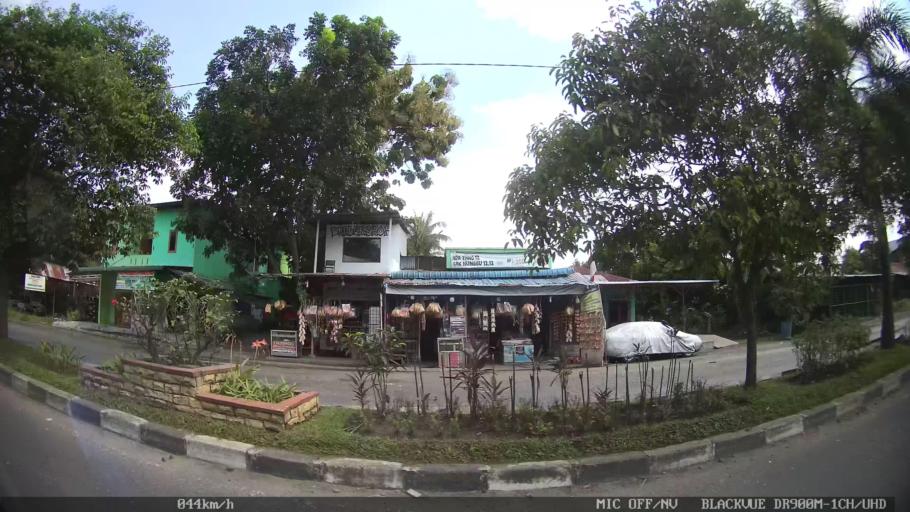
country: ID
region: North Sumatra
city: Binjai
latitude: 3.6504
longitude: 98.5104
